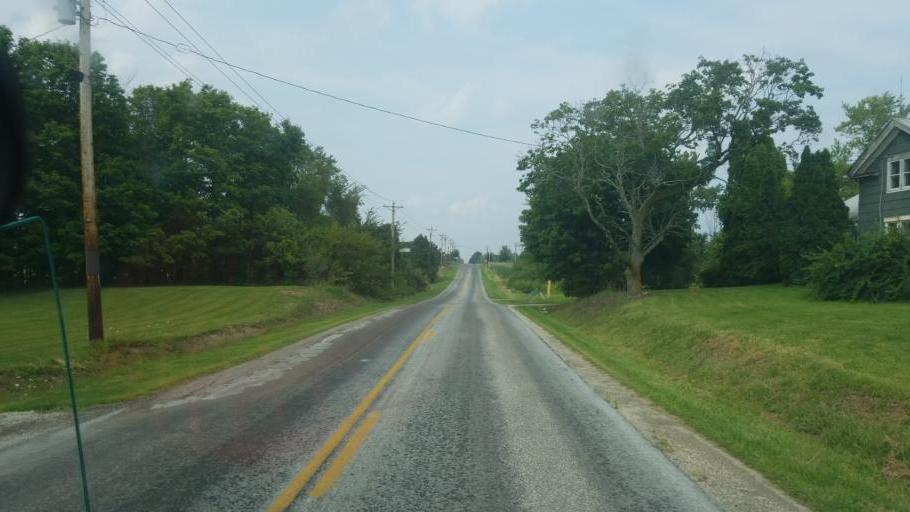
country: US
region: Ohio
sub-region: Wayne County
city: West Salem
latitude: 41.0667
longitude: -82.1622
